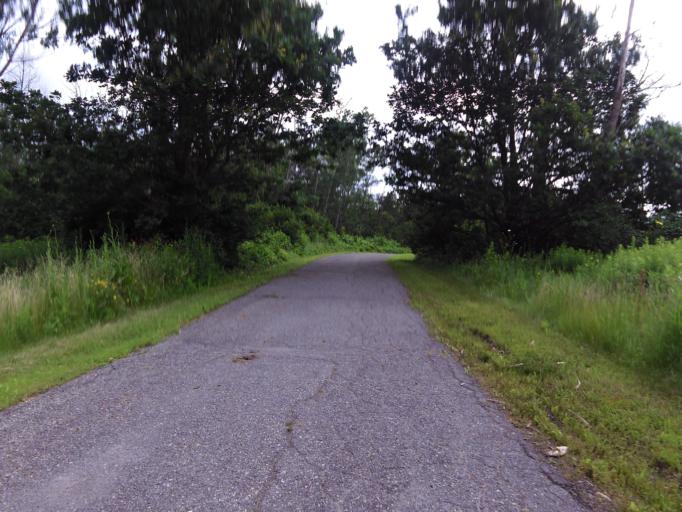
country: CA
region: Ontario
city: Bells Corners
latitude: 45.3586
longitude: -75.7740
